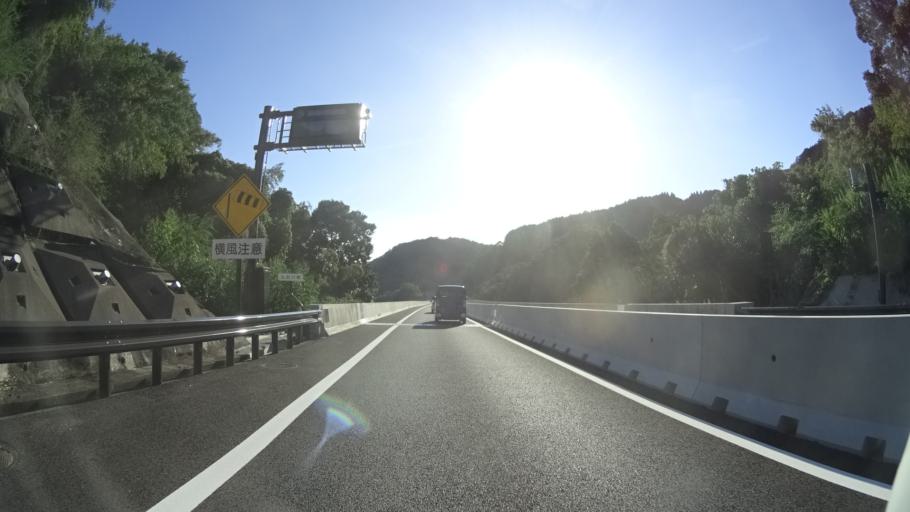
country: JP
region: Kumamoto
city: Ozu
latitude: 32.7491
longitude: 130.8492
